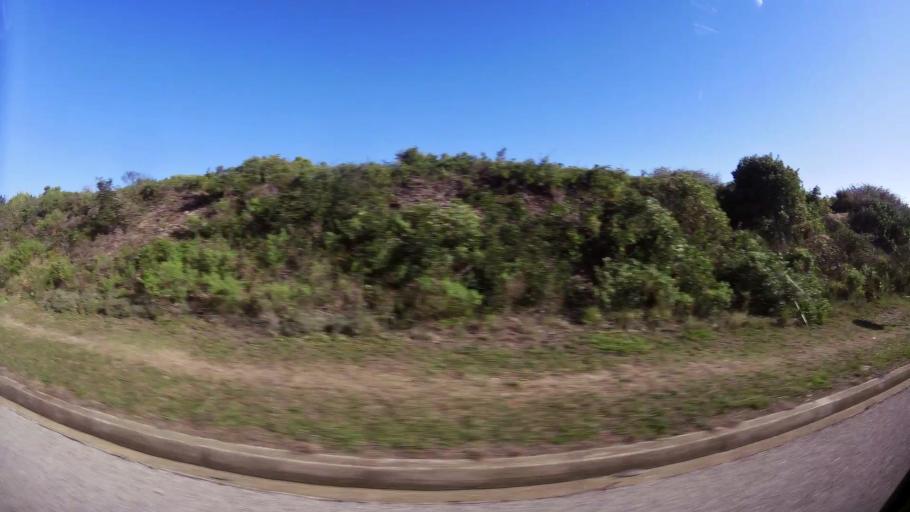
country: ZA
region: Eastern Cape
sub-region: Nelson Mandela Bay Metropolitan Municipality
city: Port Elizabeth
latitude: -33.9745
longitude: 25.6372
